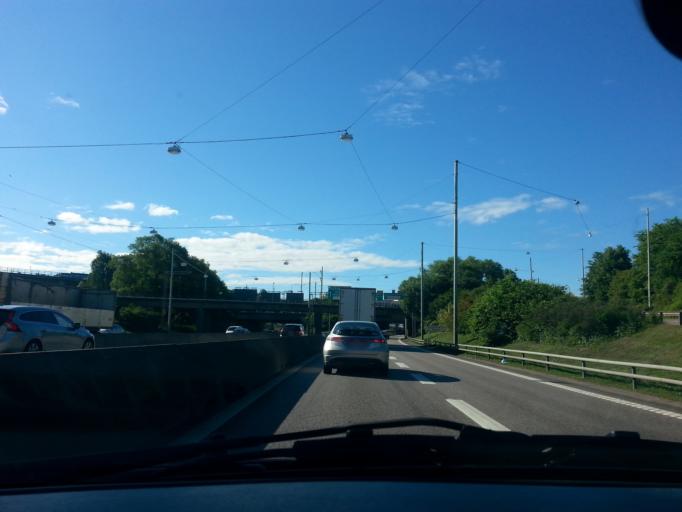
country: SE
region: Vaestra Goetaland
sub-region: Goteborg
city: Goeteborg
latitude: 57.7174
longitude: 11.9924
